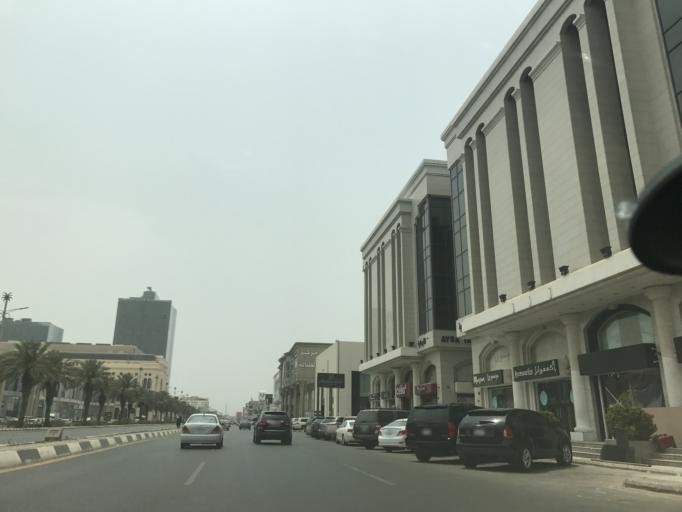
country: SA
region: Makkah
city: Jeddah
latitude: 21.5539
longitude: 39.1664
